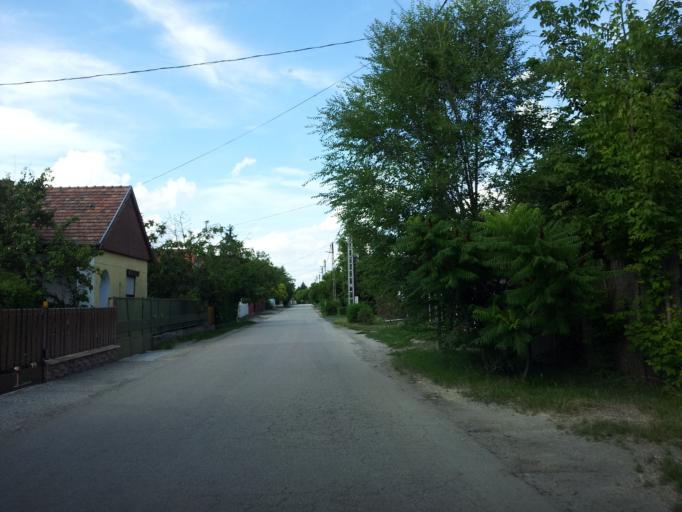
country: HU
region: Pest
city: Szigetcsep
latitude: 47.2628
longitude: 18.9895
